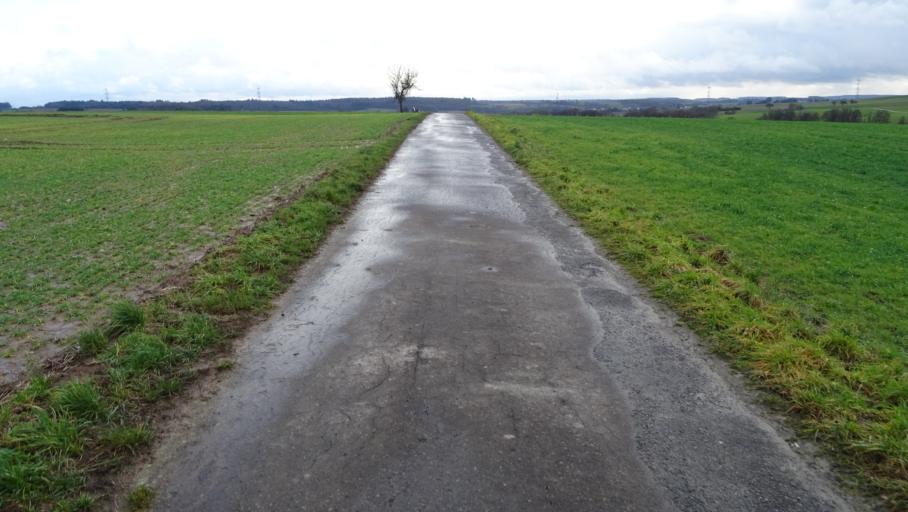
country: DE
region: Baden-Wuerttemberg
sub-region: Karlsruhe Region
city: Seckach
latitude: 49.4398
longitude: 9.2803
